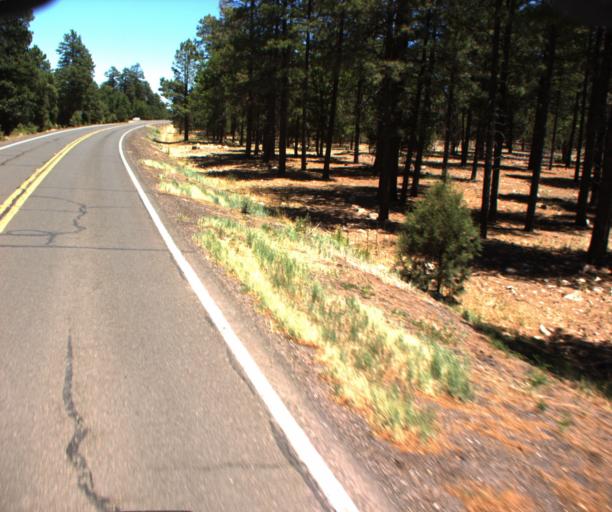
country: US
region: Arizona
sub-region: Gila County
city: Pine
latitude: 34.6138
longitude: -111.1862
